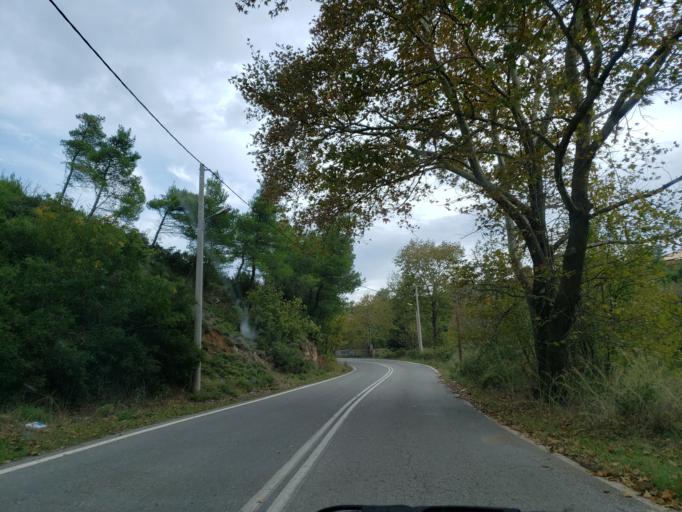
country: GR
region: Attica
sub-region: Nomarchia Anatolikis Attikis
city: Varnavas
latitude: 38.2206
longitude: 23.9312
